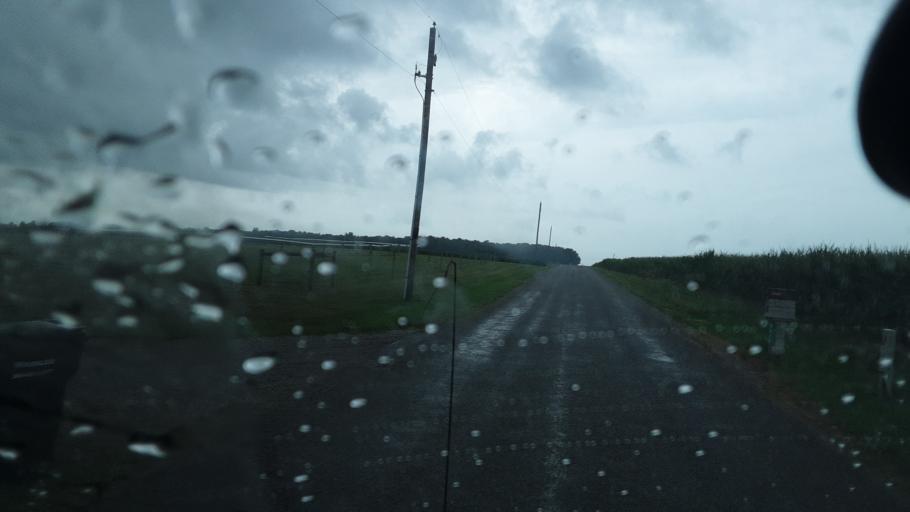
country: US
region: Indiana
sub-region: Steuben County
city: Hamilton
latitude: 41.5373
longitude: -84.8201
